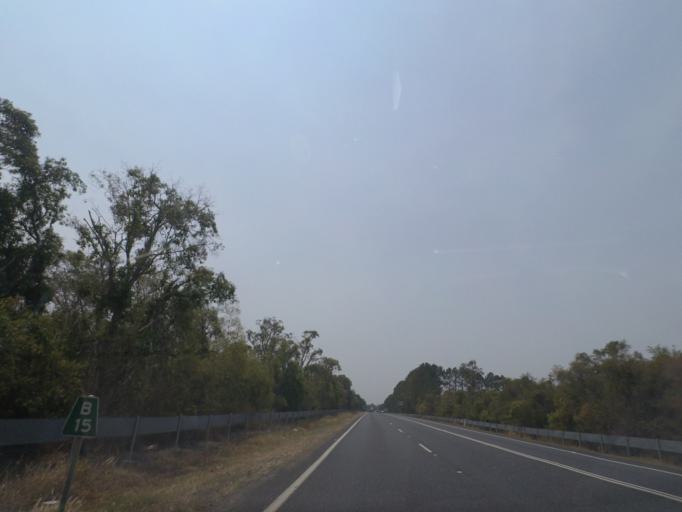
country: AU
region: New South Wales
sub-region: Ballina
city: Ballina
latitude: -28.9428
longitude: 153.4686
